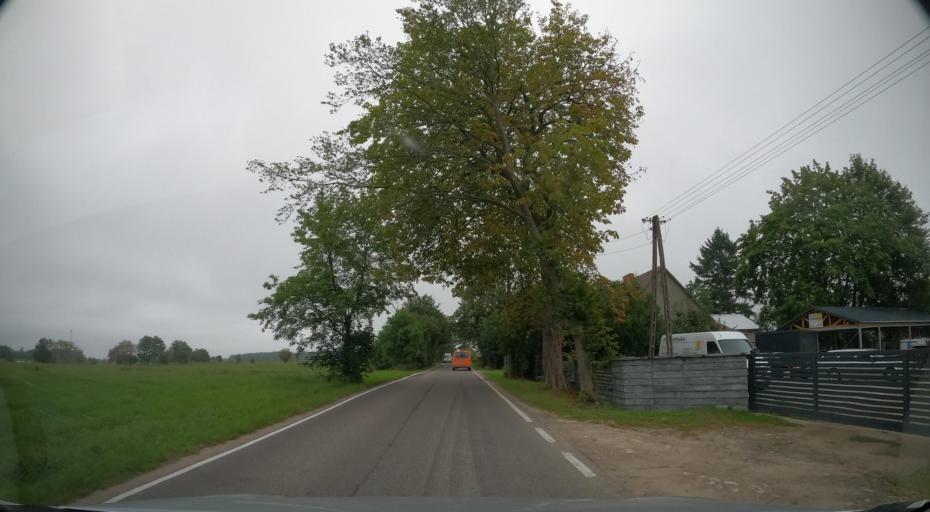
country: PL
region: Pomeranian Voivodeship
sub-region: Powiat wejherowski
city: Szemud
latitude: 54.5021
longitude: 18.1536
